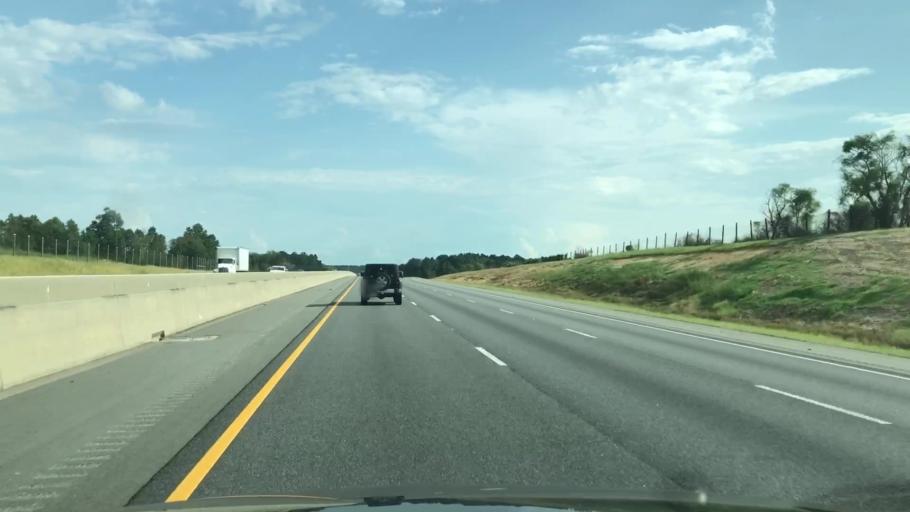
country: US
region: Georgia
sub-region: Tift County
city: Tifton
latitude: 31.5302
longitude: -83.5224
